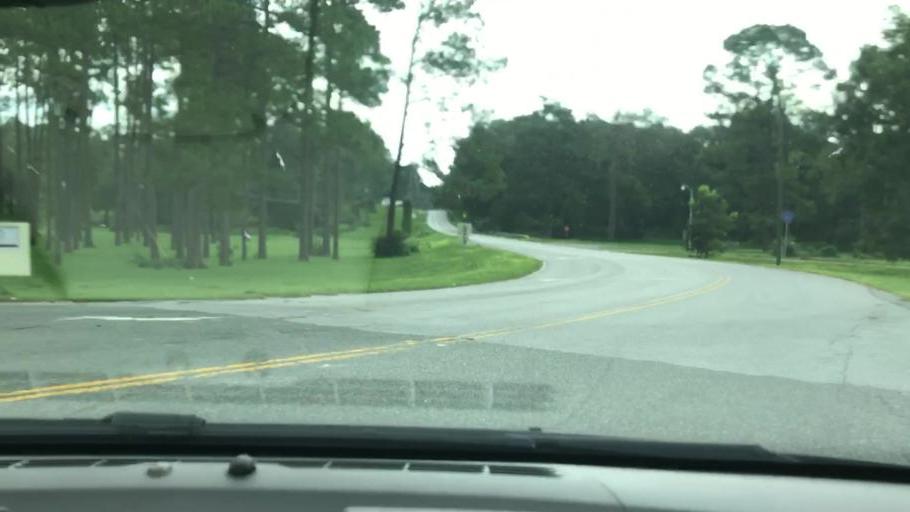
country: US
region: Florida
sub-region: Jackson County
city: Marianna
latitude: 30.7640
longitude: -85.2544
